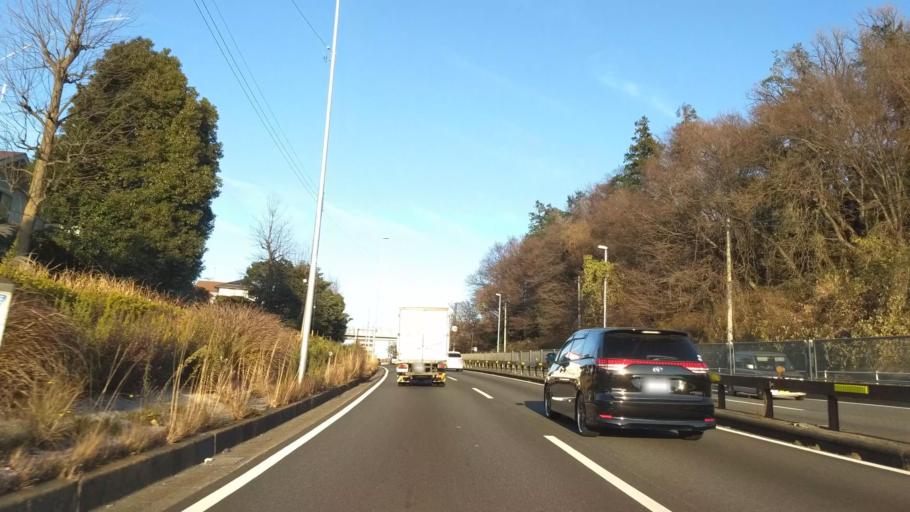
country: JP
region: Kanagawa
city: Zama
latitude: 35.4653
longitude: 139.4048
